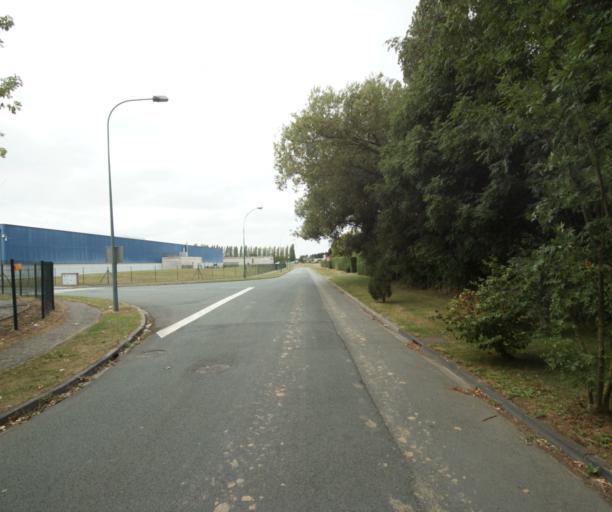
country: FR
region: Nord-Pas-de-Calais
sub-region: Departement du Nord
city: Toufflers
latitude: 50.6688
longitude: 3.2402
